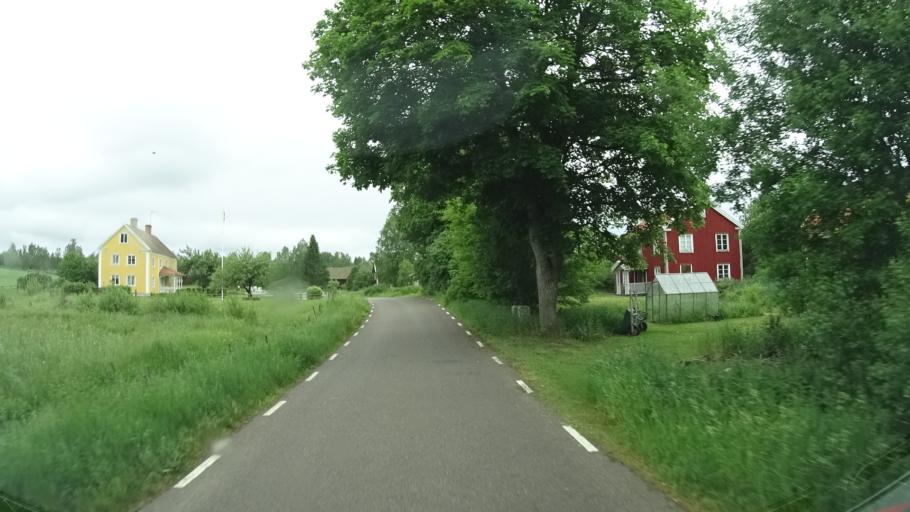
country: SE
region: Kalmar
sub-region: Vimmerby Kommun
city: Sodra Vi
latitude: 57.6939
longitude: 15.6947
